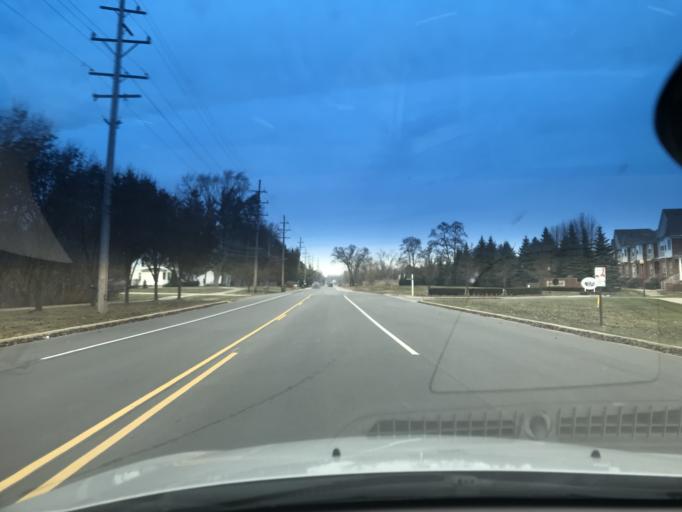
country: US
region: Michigan
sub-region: Macomb County
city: Shelby
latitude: 42.7014
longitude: -83.0546
